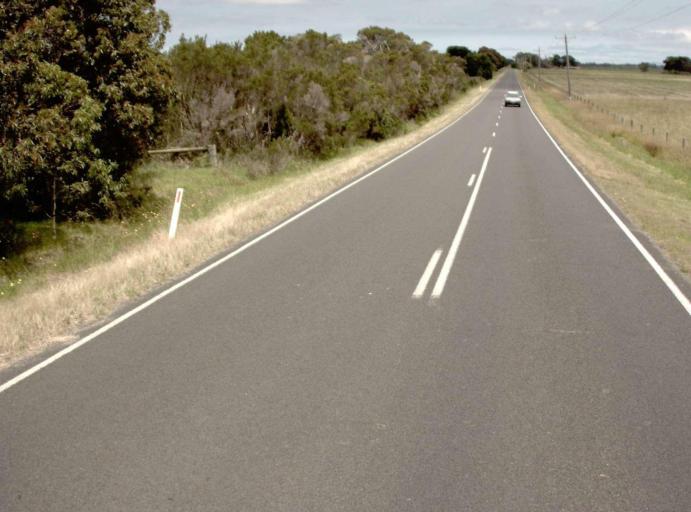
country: AU
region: Victoria
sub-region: Latrobe
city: Traralgon
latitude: -38.5432
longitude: 146.6561
